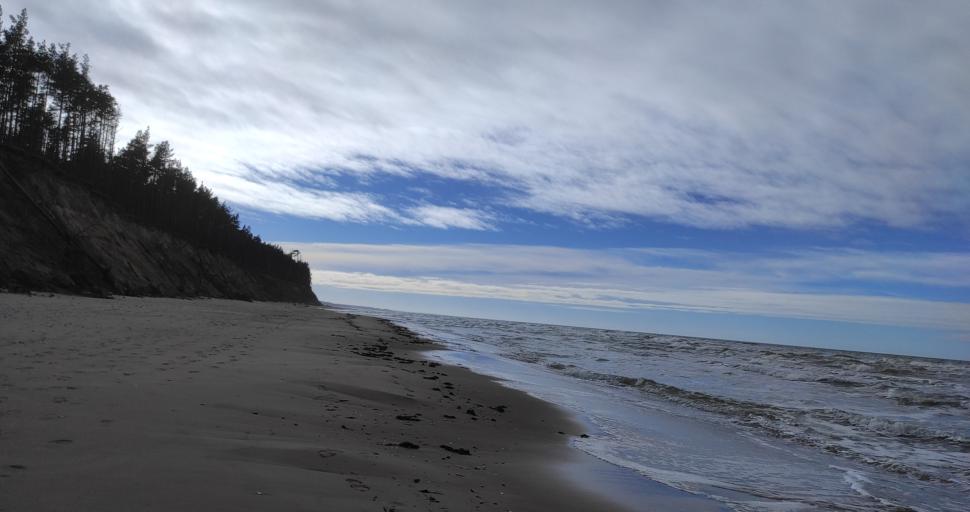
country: LV
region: Alsunga
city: Alsunga
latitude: 57.0238
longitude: 21.3917
